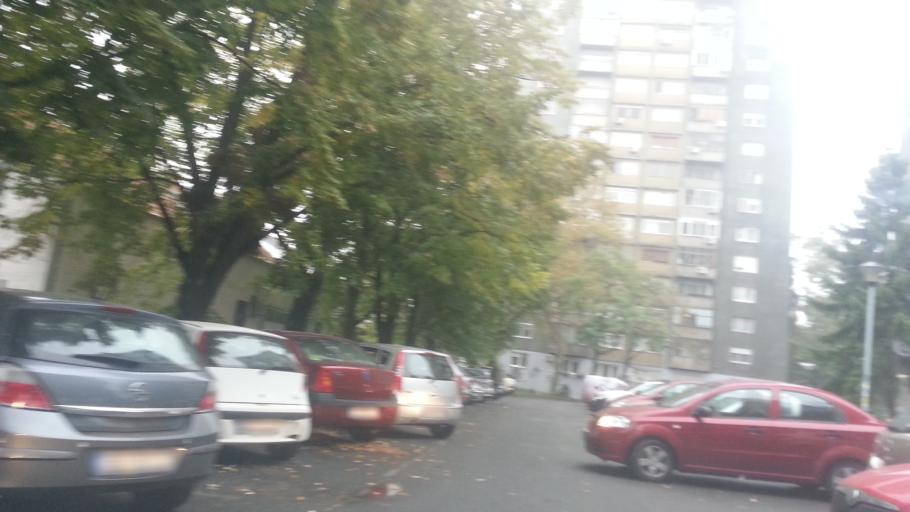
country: RS
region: Central Serbia
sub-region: Belgrade
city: Zemun
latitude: 44.8354
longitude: 20.4078
